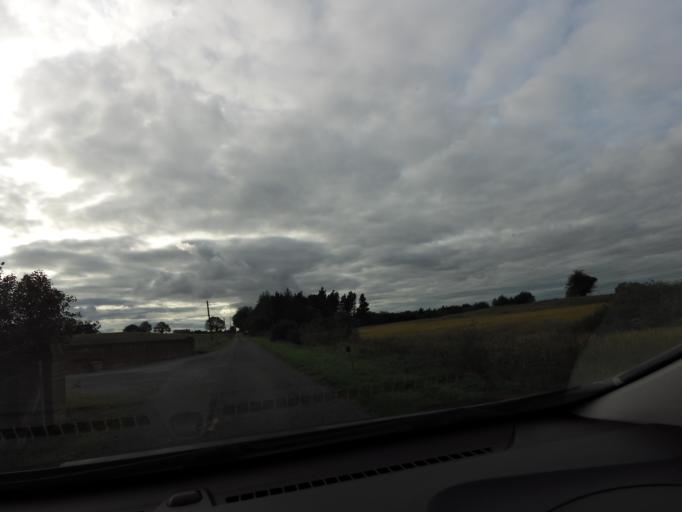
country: IE
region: Connaught
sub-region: County Galway
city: Ballinasloe
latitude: 53.3649
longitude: -8.1273
